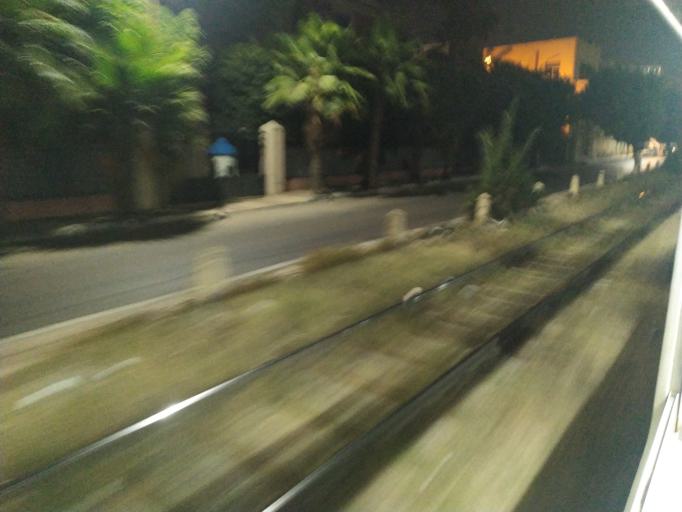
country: EG
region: Alexandria
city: Alexandria
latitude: 31.2084
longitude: 29.9151
